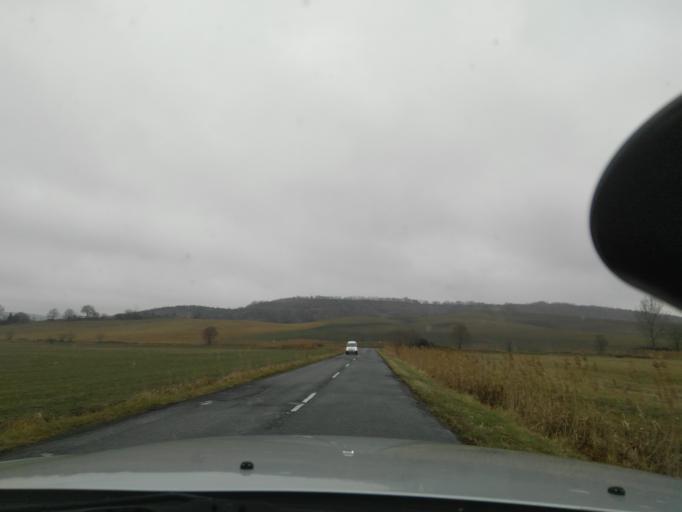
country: HU
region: Nograd
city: Kazar
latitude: 48.0386
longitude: 19.8752
